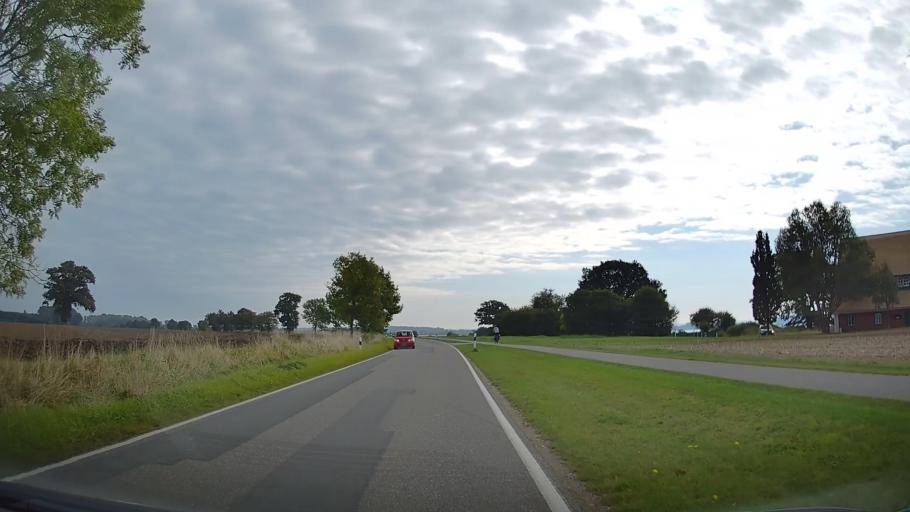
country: DE
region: Schleswig-Holstein
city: Panker
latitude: 54.3401
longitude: 10.6196
